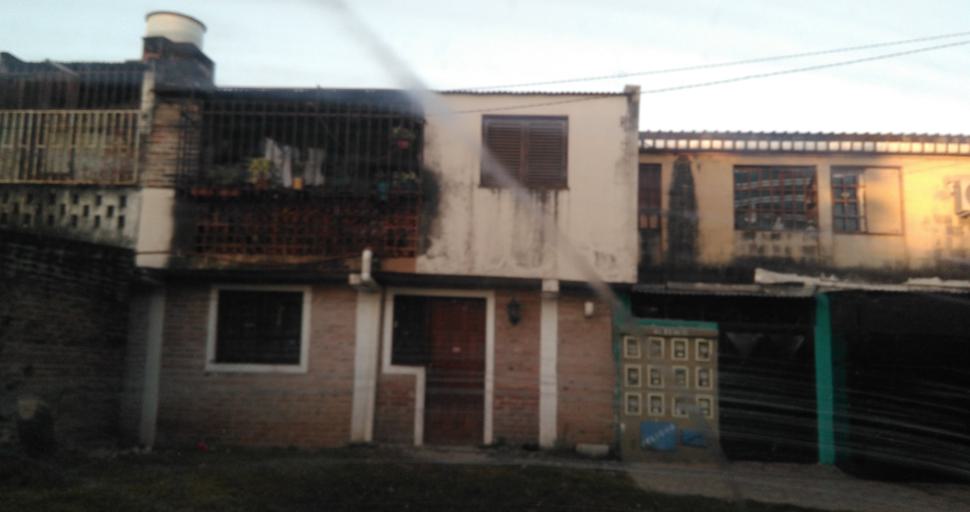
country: AR
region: Chaco
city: Resistencia
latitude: -27.4623
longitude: -59.0160
